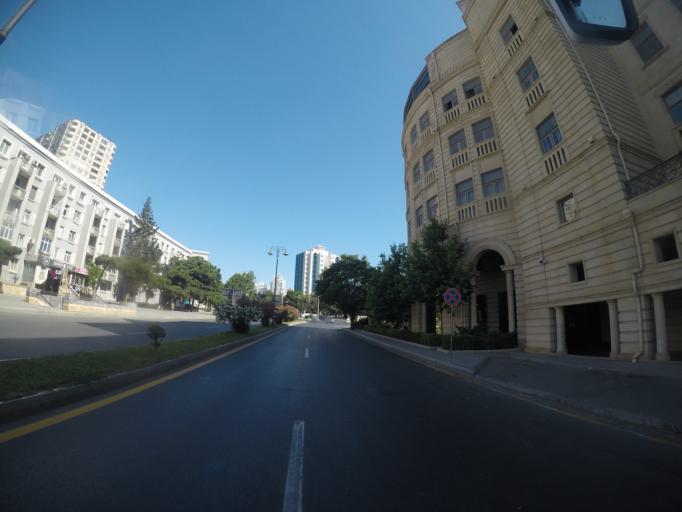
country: AZ
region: Baki
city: Badamdar
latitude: 40.3908
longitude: 49.8230
